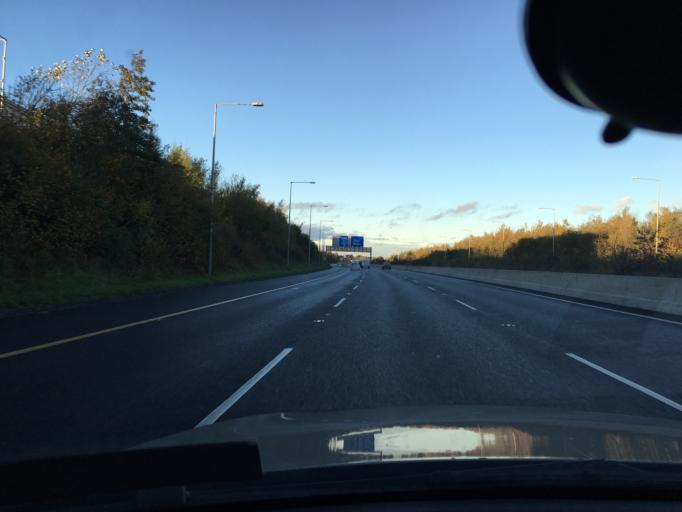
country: IE
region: Leinster
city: Kinsealy-Drinan
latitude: 53.4541
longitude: -6.2030
